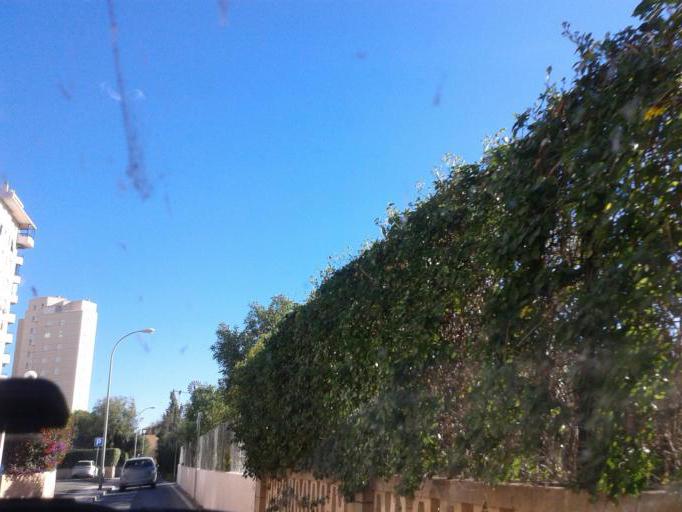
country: ES
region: Valencia
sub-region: Provincia de Alicante
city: San Juan de Alicante
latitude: 38.4022
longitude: -0.4085
